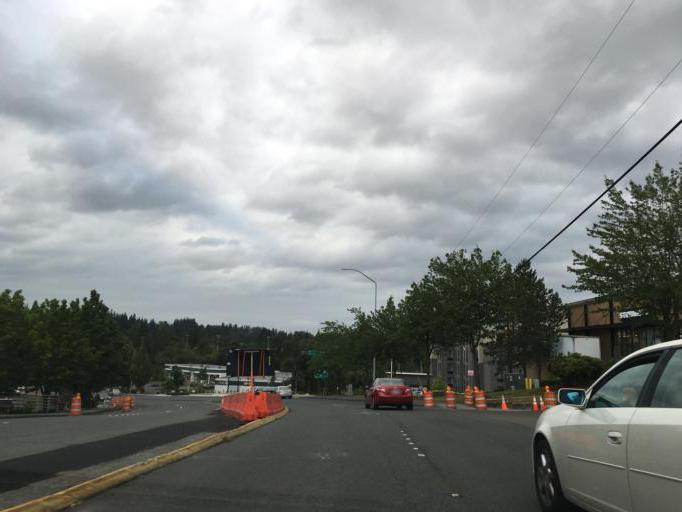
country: US
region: Washington
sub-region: Snohomish County
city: Alderwood Manor
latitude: 47.8328
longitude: -122.2685
